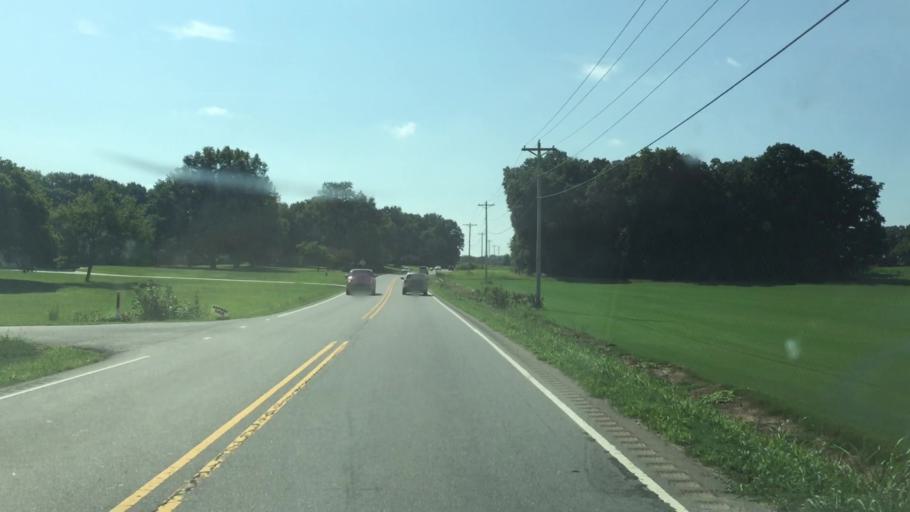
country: US
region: North Carolina
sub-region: Union County
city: Fairview
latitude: 35.1451
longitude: -80.5507
